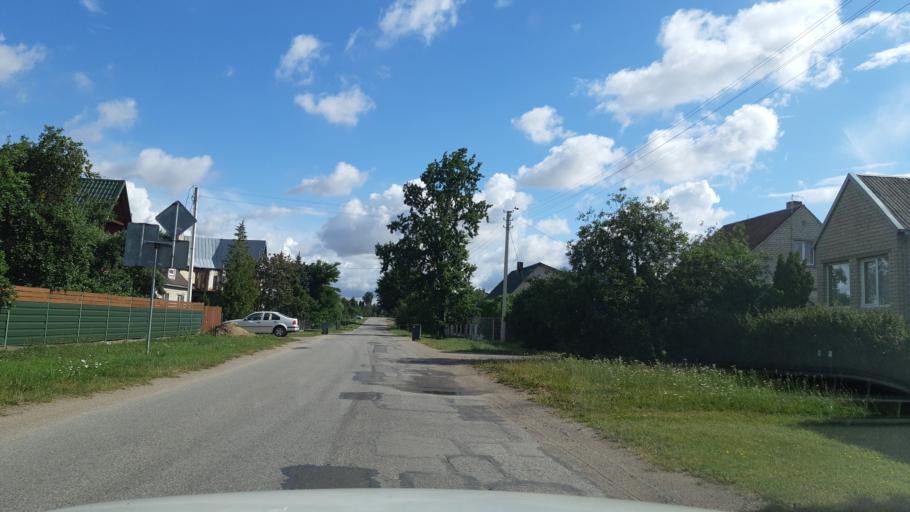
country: LT
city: Vilkaviskis
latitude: 54.6366
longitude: 23.0534
